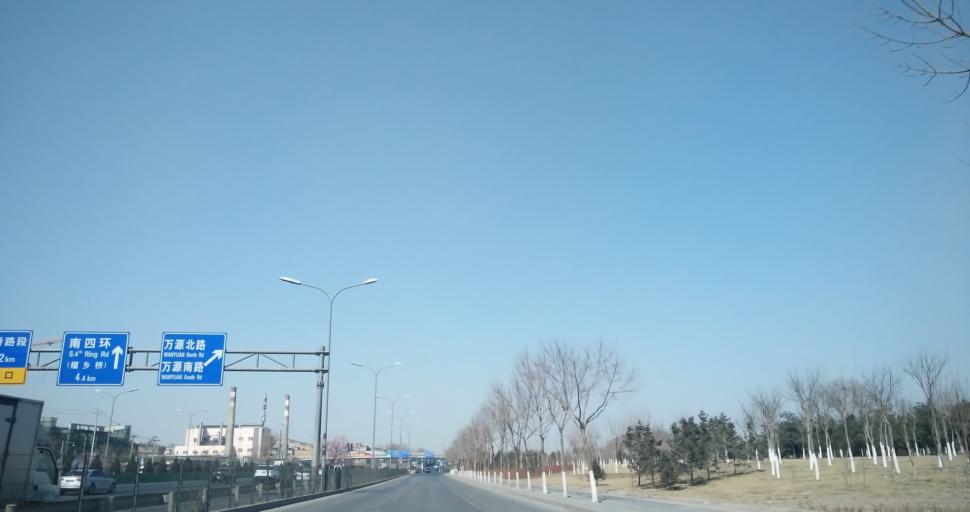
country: CN
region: Beijing
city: Jiugong
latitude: 39.7908
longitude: 116.4242
